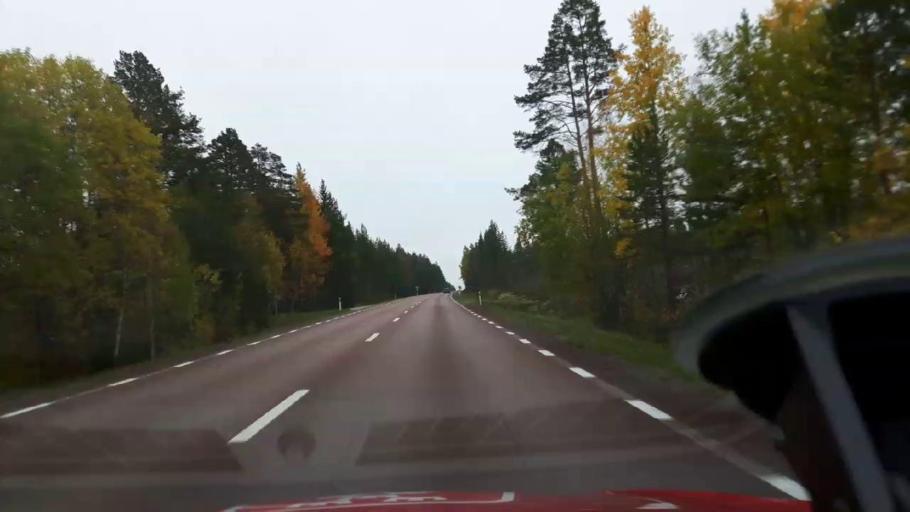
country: SE
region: Jaemtland
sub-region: Bergs Kommun
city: Hoverberg
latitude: 62.4502
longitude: 14.5608
